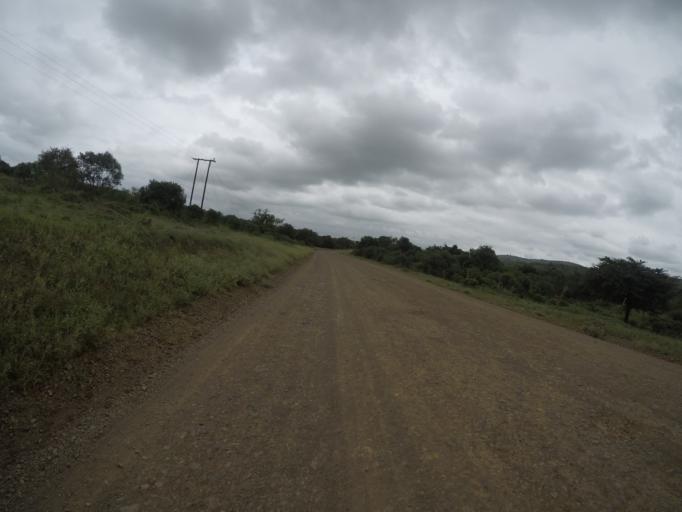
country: ZA
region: KwaZulu-Natal
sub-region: uThungulu District Municipality
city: Empangeni
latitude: -28.5933
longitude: 31.8367
